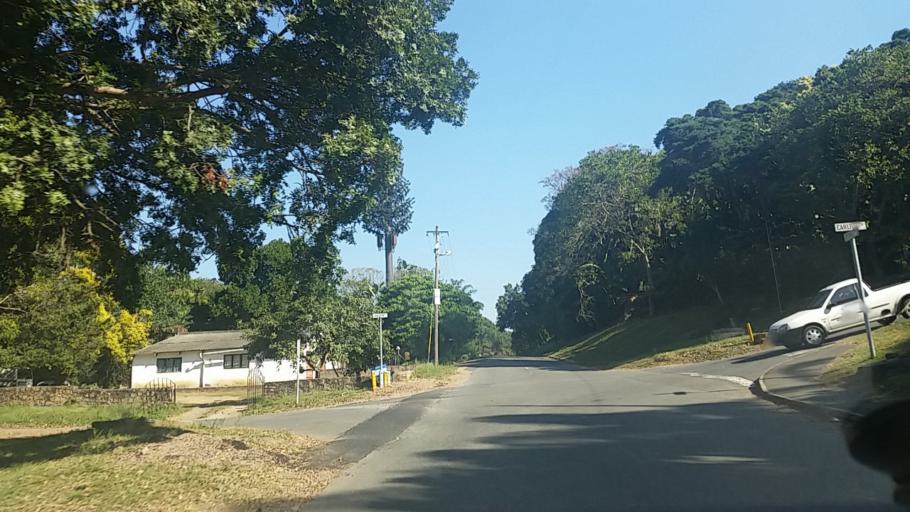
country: ZA
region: KwaZulu-Natal
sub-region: eThekwini Metropolitan Municipality
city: Berea
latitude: -29.8482
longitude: 30.9032
